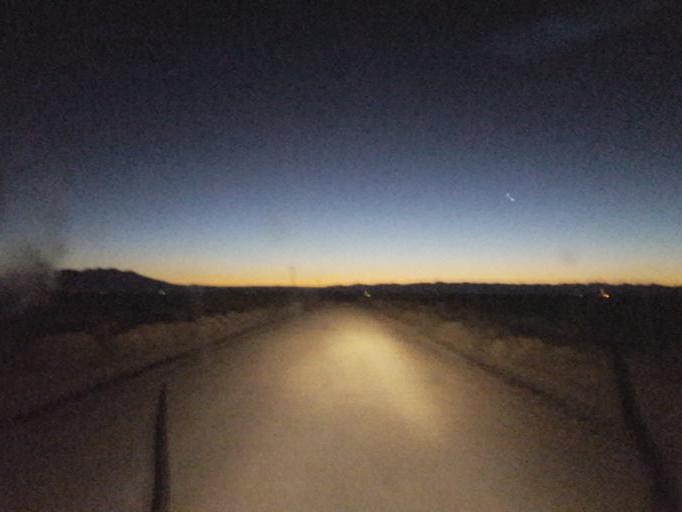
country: US
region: Colorado
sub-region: Rio Grande County
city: Monte Vista
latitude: 37.4011
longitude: -106.1054
